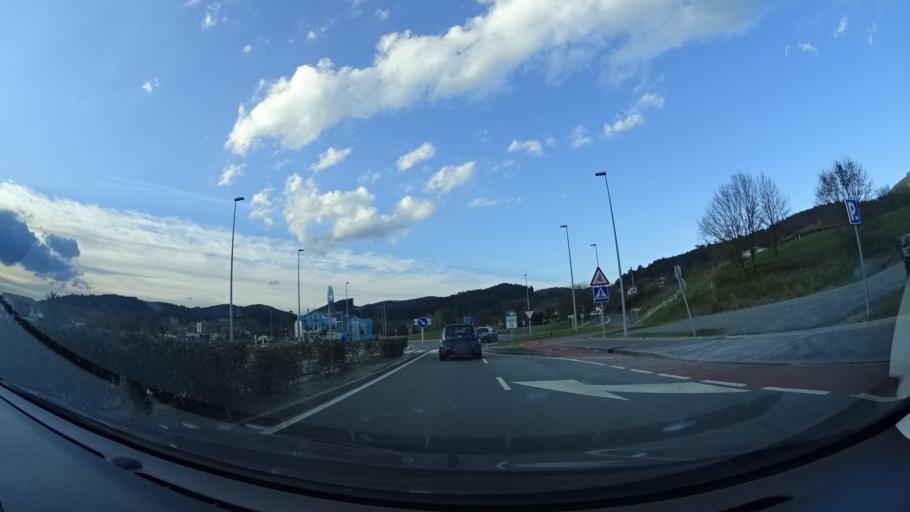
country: ES
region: Basque Country
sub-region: Bizkaia
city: Gatika
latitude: 43.3807
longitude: -2.8690
